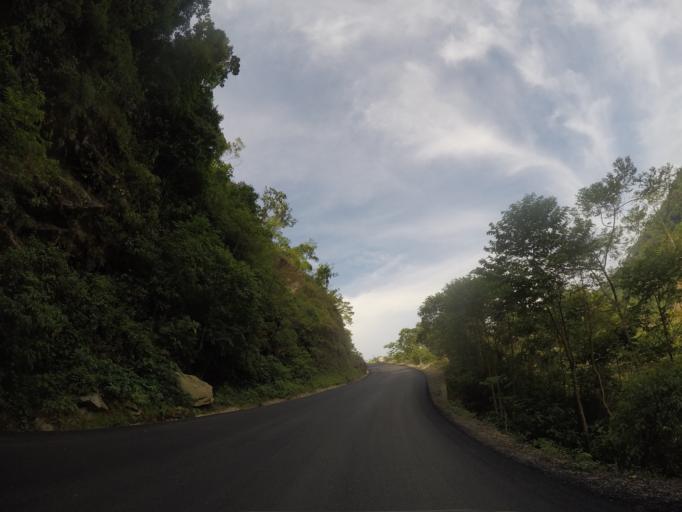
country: MX
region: Oaxaca
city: Pluma Hidalgo
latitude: 15.9386
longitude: -96.4308
